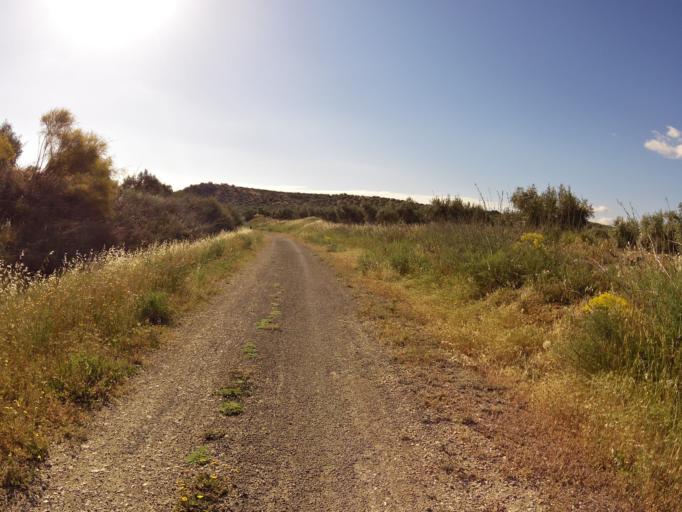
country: ES
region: Andalusia
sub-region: Province of Cordoba
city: Luque
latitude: 37.5823
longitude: -4.1969
